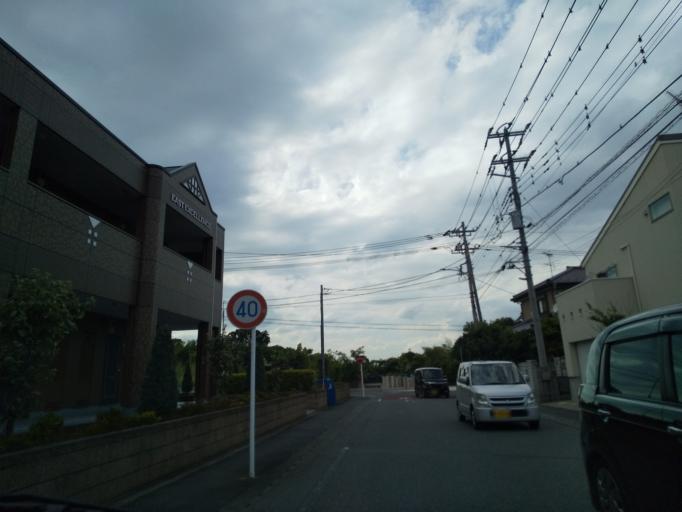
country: JP
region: Chiba
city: Noda
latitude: 35.9922
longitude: 139.8126
